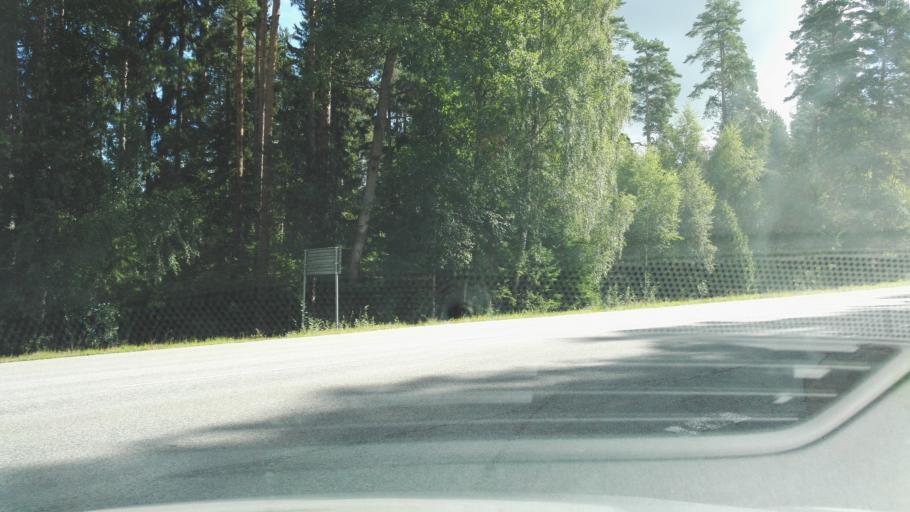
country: SE
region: Kronoberg
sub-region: Vaxjo Kommun
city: Gemla
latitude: 56.8578
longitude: 14.6920
